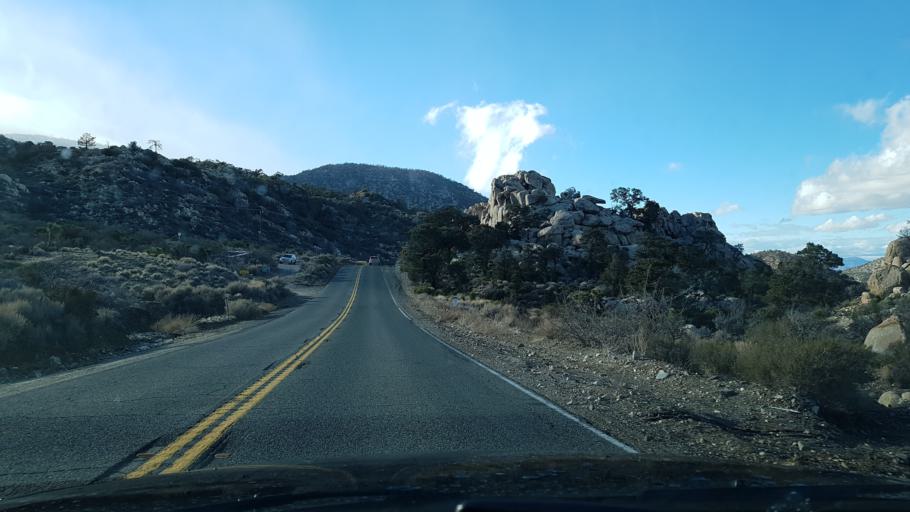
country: US
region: California
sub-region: San Bernardino County
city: Big Bear City
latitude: 34.3170
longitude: -116.8141
